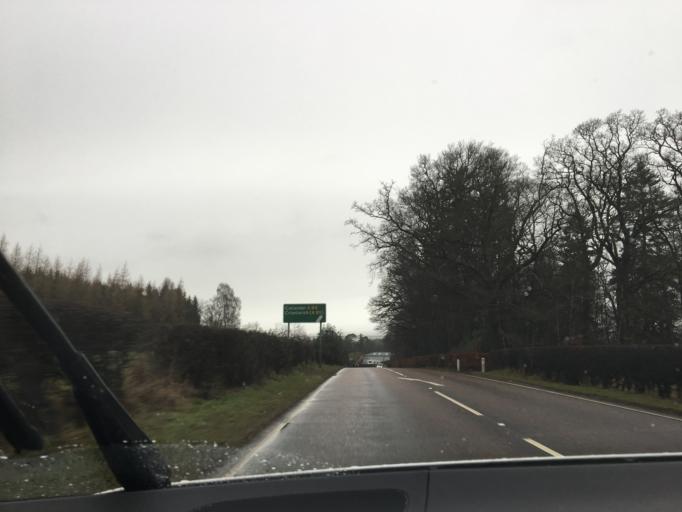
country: GB
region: Scotland
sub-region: Stirling
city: Doune
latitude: 56.1801
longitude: -4.0643
